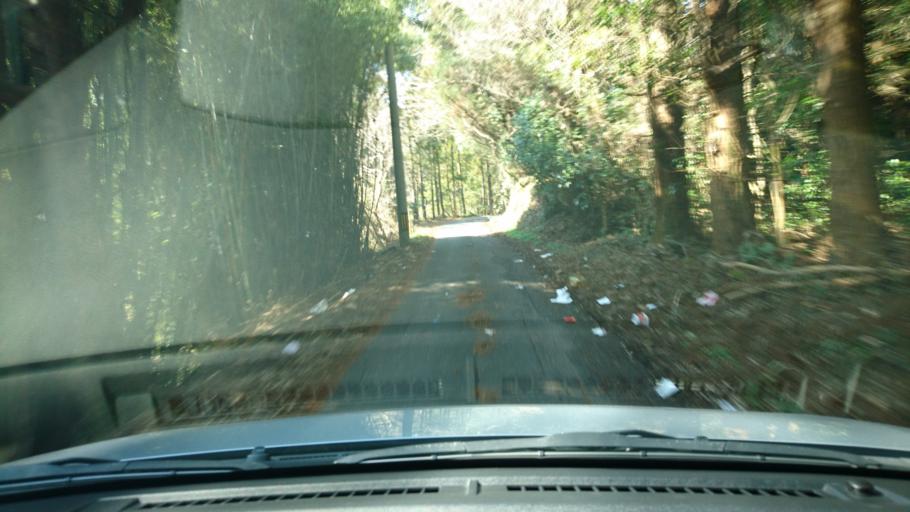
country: JP
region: Miyazaki
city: Miyazaki-shi
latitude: 31.8276
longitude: 131.3946
